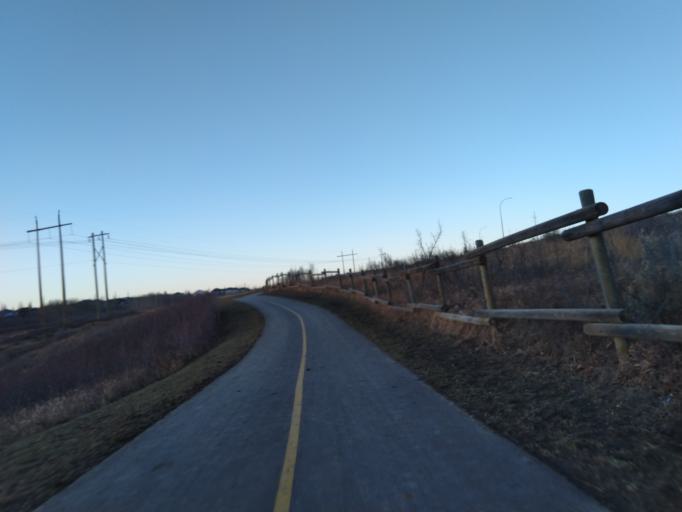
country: CA
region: Alberta
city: Calgary
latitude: 51.1159
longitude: -114.2332
